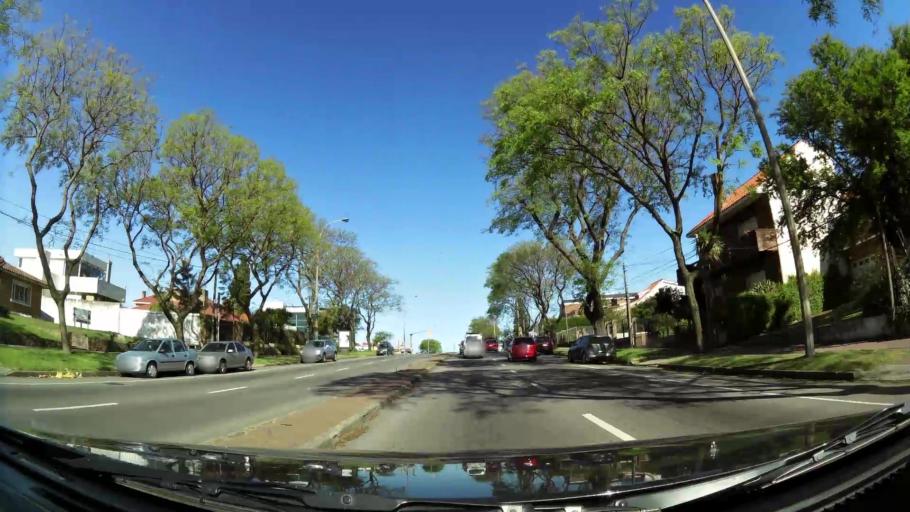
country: UY
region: Canelones
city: Paso de Carrasco
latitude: -34.8958
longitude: -56.0817
